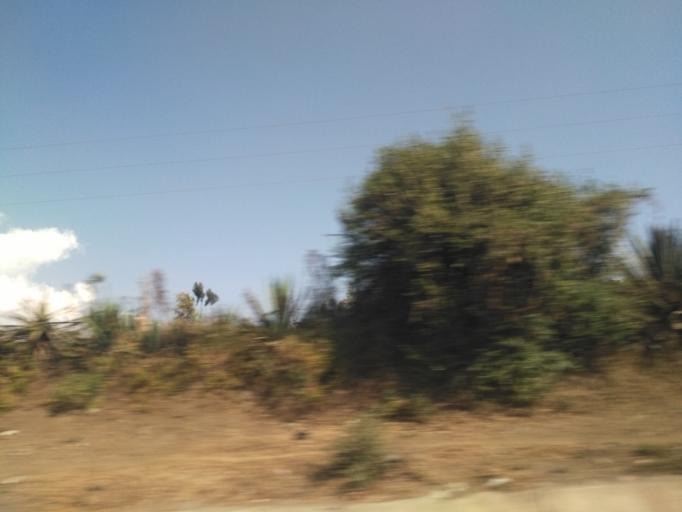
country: TZ
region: Arusha
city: Arusha
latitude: -3.2183
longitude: 36.6073
